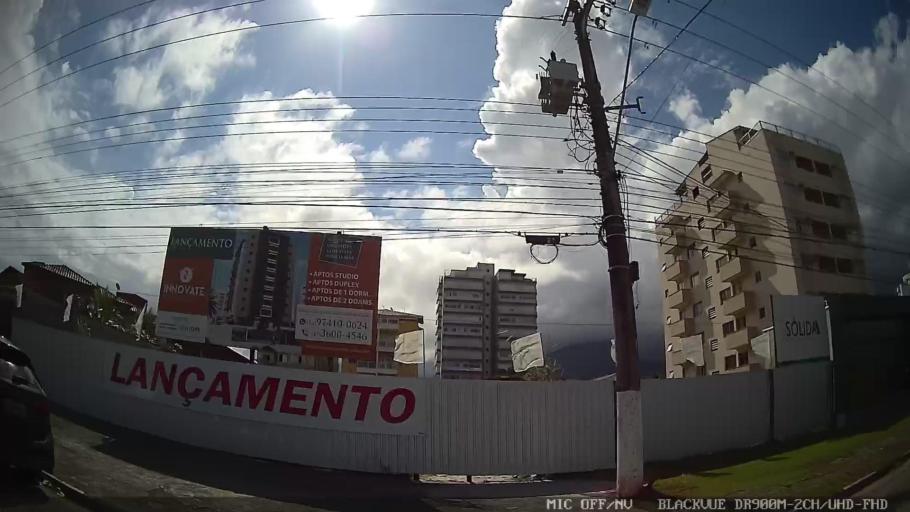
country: BR
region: Sao Paulo
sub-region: Caraguatatuba
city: Caraguatatuba
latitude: -23.6408
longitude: -45.4231
